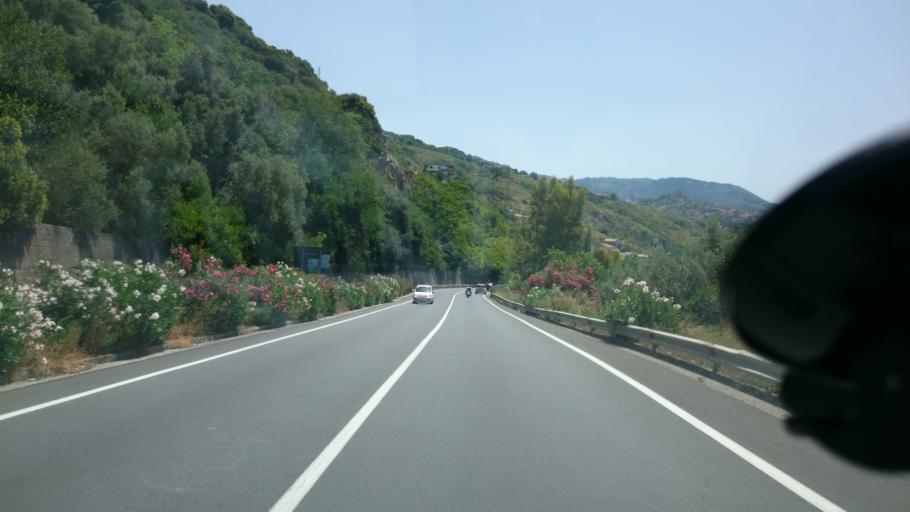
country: IT
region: Calabria
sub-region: Provincia di Cosenza
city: Cetraro Marina
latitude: 39.5301
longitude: 15.9226
